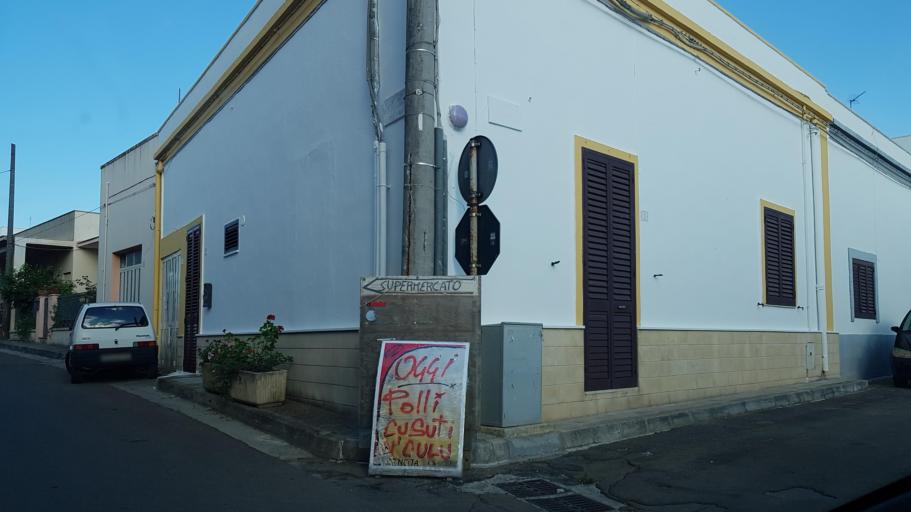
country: IT
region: Apulia
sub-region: Provincia di Lecce
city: Castiglione
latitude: 39.9822
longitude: 18.3493
